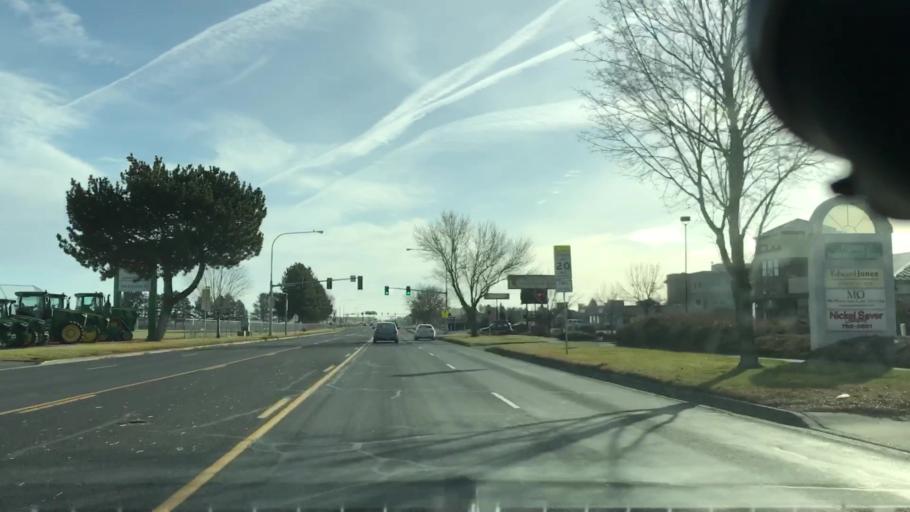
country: US
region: Washington
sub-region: Grant County
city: Moses Lake
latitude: 47.1140
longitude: -119.2613
